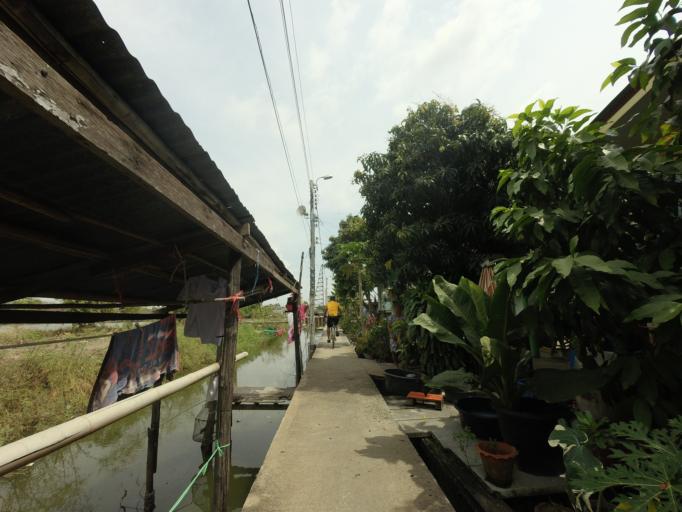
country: TH
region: Bangkok
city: Lat Krabang
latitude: 13.6673
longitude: 100.7638
